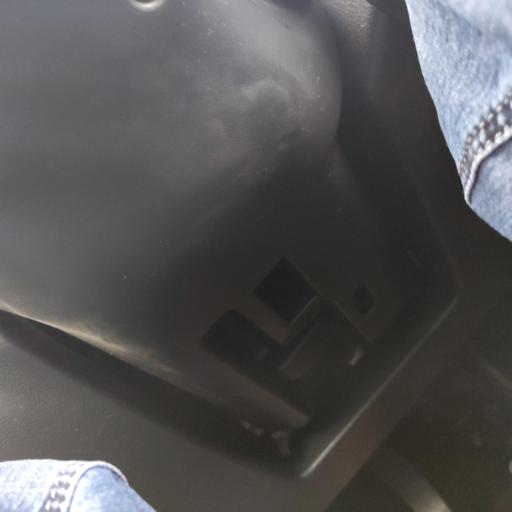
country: RU
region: Samara
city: Smyshlyayevka
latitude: 53.2113
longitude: 50.3275
